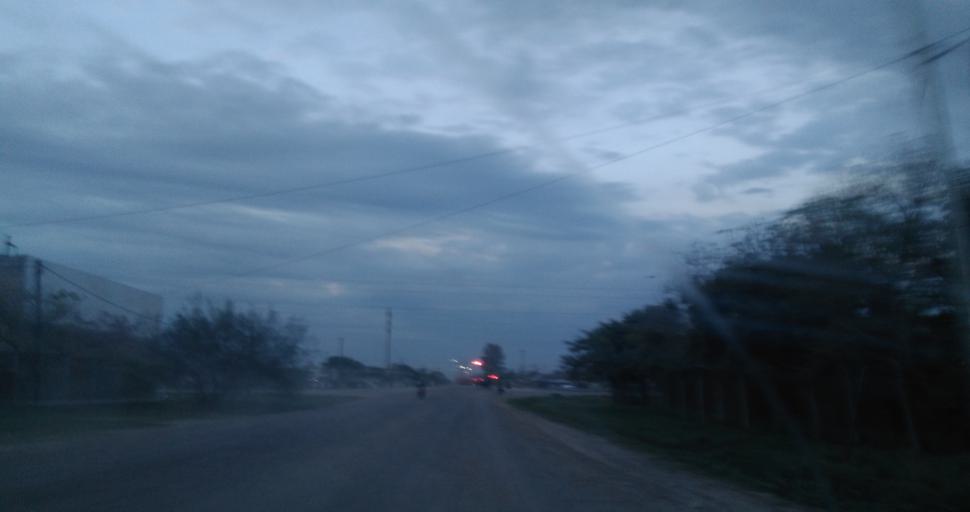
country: AR
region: Chaco
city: Resistencia
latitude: -27.4804
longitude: -58.9995
